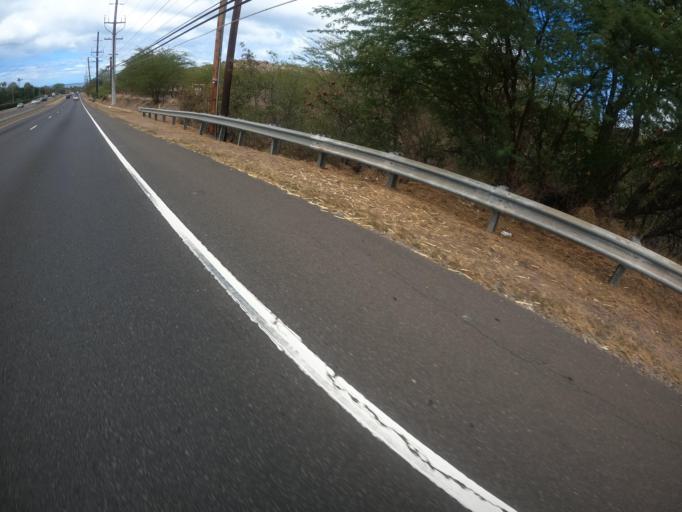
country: US
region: Hawaii
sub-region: Honolulu County
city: Makakilo City
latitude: 21.3442
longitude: -158.1147
